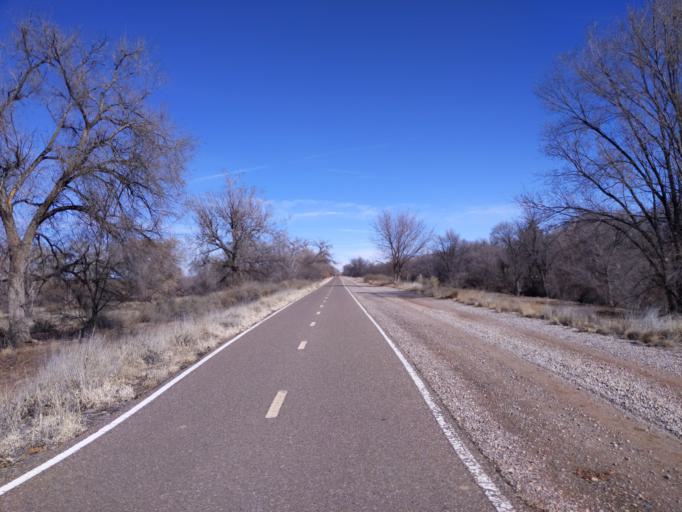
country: US
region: New Mexico
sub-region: Bernalillo County
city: Lee Acres
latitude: 35.1494
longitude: -106.6715
